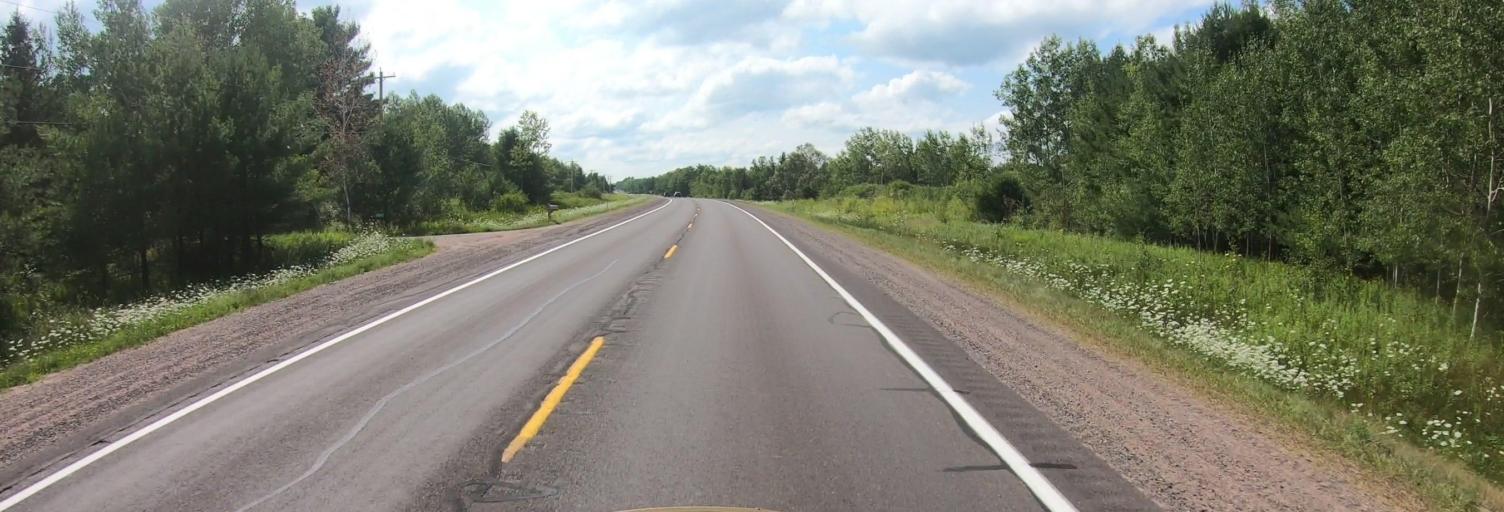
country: US
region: Michigan
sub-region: Ontonagon County
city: Ontonagon
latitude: 46.5346
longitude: -89.2119
